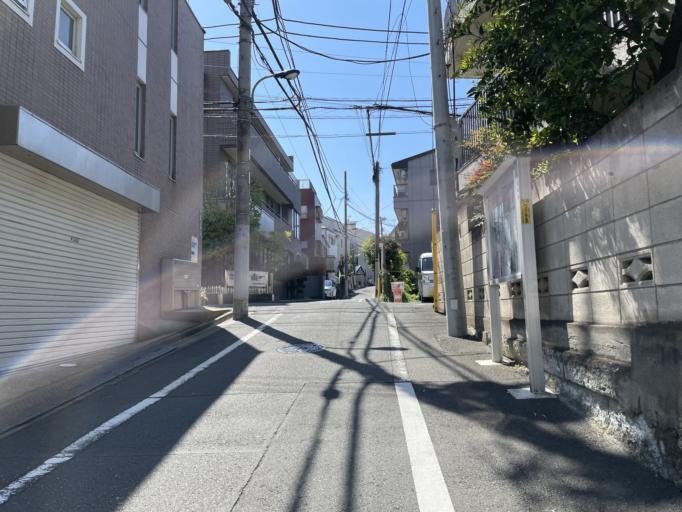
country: JP
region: Saitama
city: Kawaguchi
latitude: 35.7441
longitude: 139.7355
